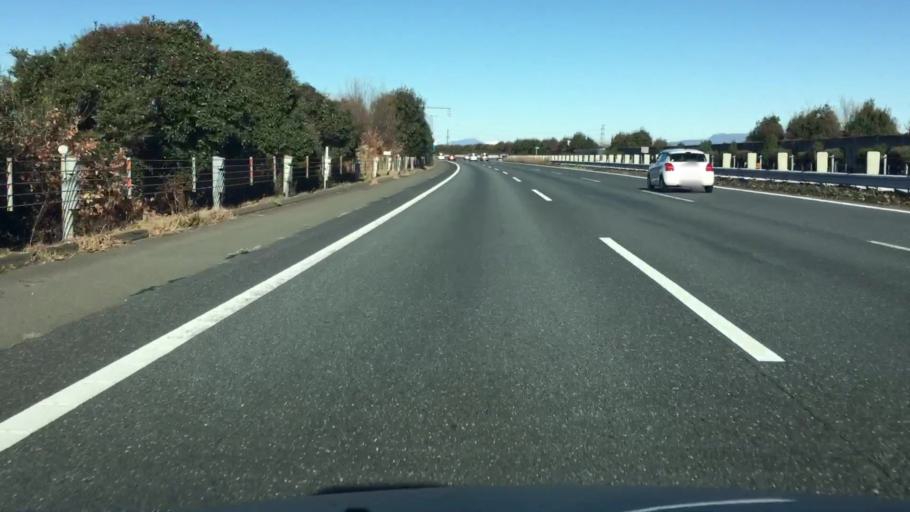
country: JP
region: Saitama
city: Honjo
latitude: 36.1919
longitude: 139.1890
